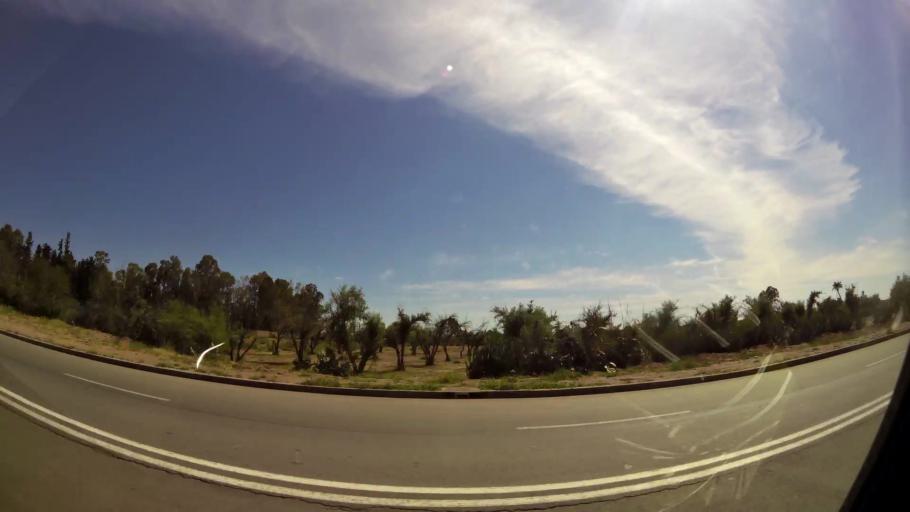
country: MA
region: Marrakech-Tensift-Al Haouz
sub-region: Marrakech
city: Marrakesh
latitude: 31.6162
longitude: -7.9525
